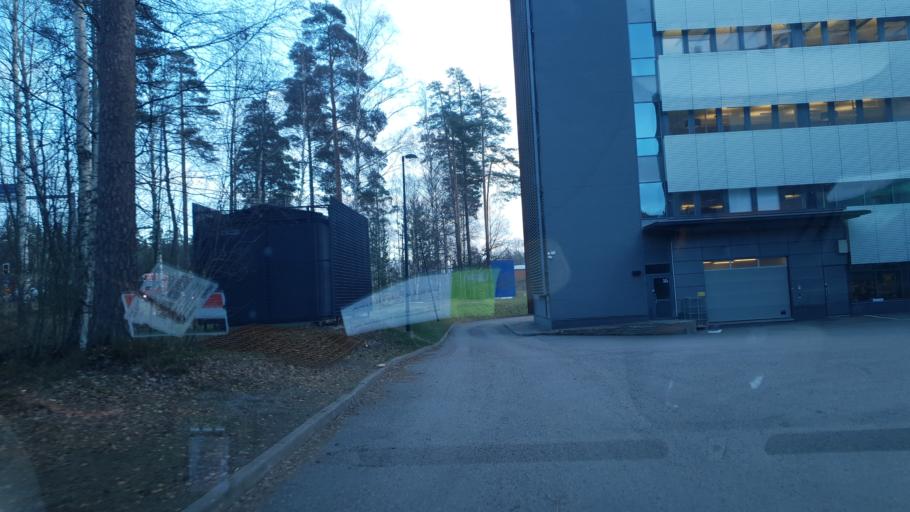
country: FI
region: Uusimaa
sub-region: Helsinki
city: Kilo
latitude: 60.2253
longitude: 24.7568
